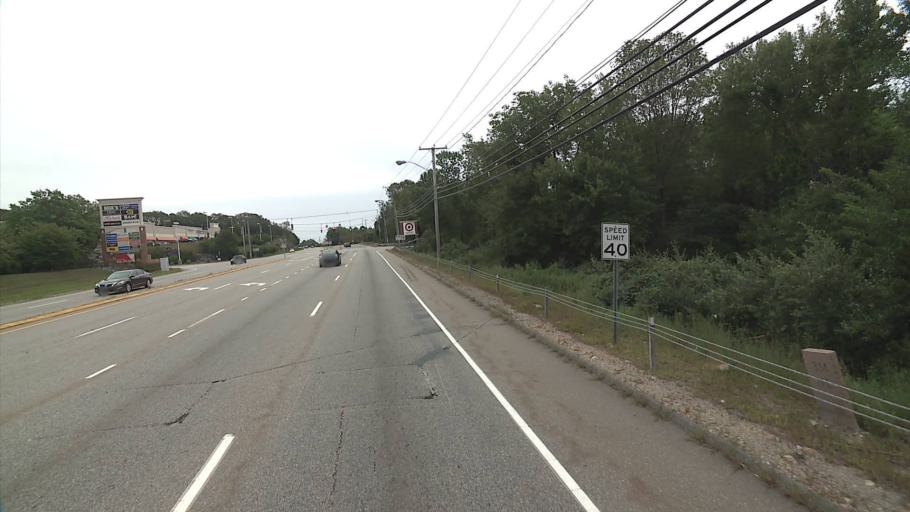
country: US
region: Connecticut
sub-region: New London County
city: Central Waterford
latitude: 41.3793
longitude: -72.1503
